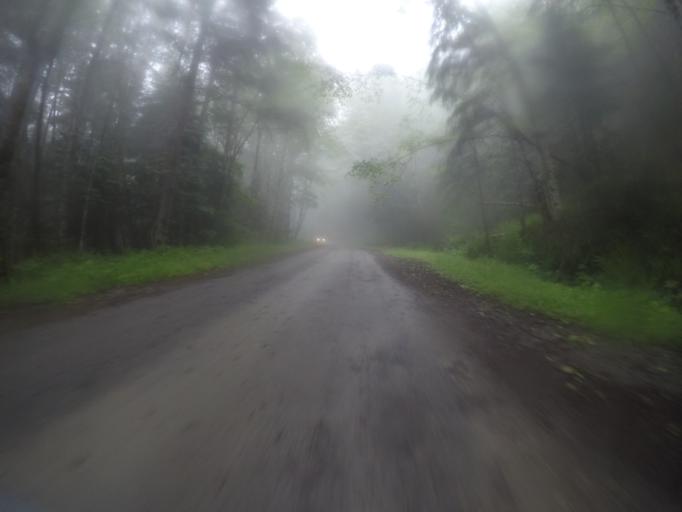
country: US
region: California
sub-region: Humboldt County
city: Westhaven-Moonstone
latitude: 41.2449
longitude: -123.9861
